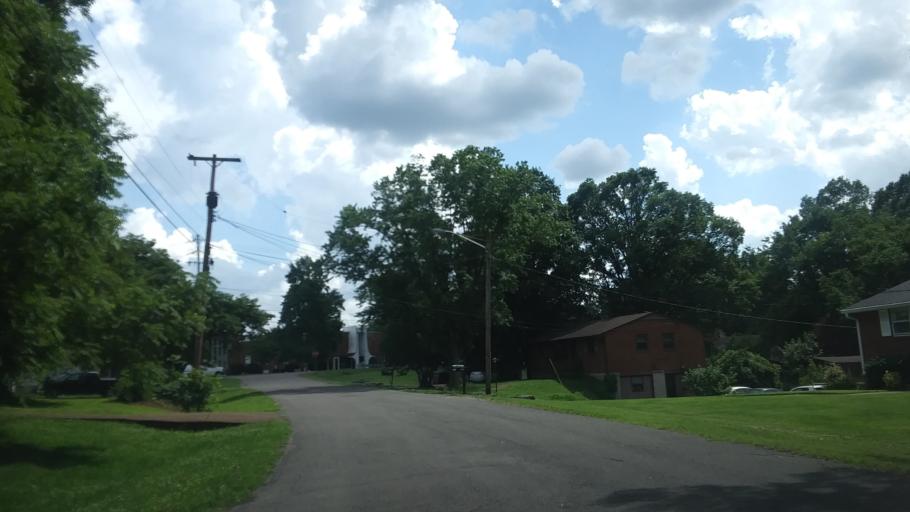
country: US
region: Tennessee
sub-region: Davidson County
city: Oak Hill
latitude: 36.0713
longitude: -86.7012
